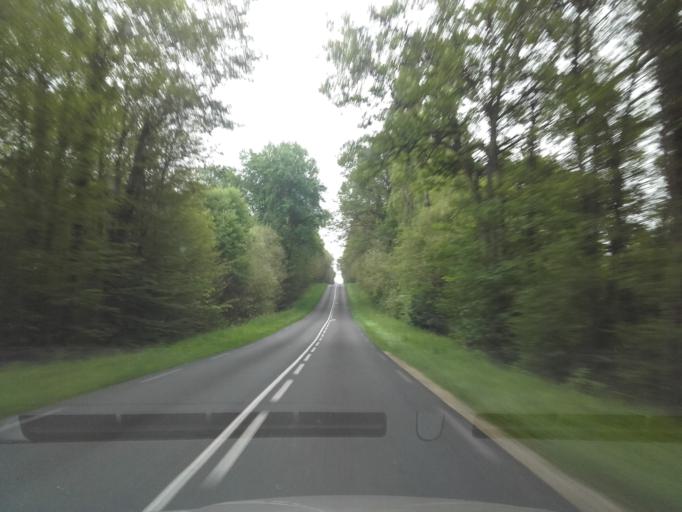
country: FR
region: Centre
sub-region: Departement d'Indre-et-Loire
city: Beaumont-la-Ronce
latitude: 47.5882
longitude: 0.6658
